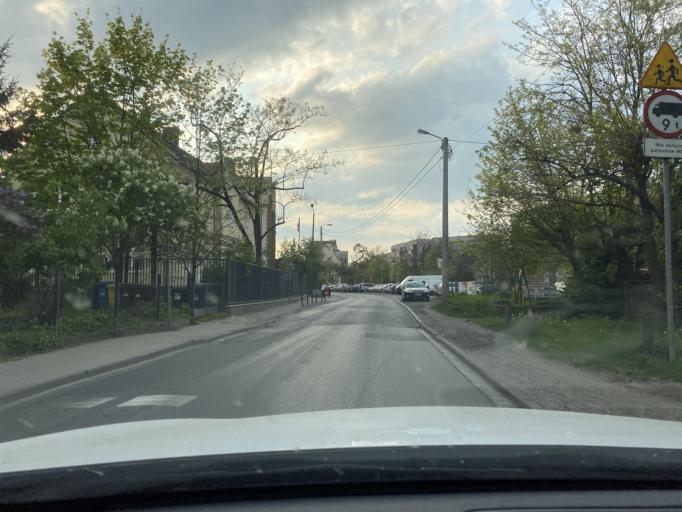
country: PL
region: Lower Silesian Voivodeship
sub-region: Powiat wroclawski
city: Wroclaw
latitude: 51.1383
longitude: 17.0673
